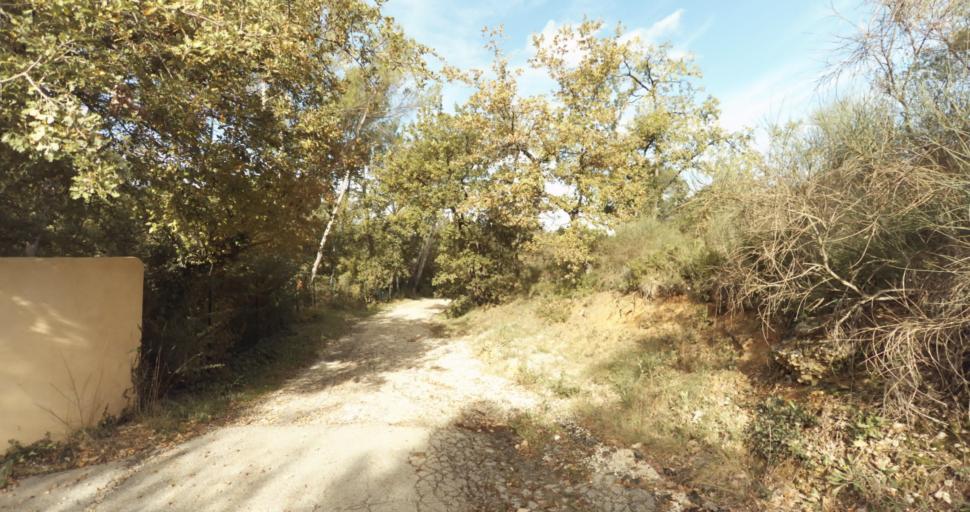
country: FR
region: Provence-Alpes-Cote d'Azur
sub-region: Departement des Bouches-du-Rhone
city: Venelles
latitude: 43.6079
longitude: 5.4859
